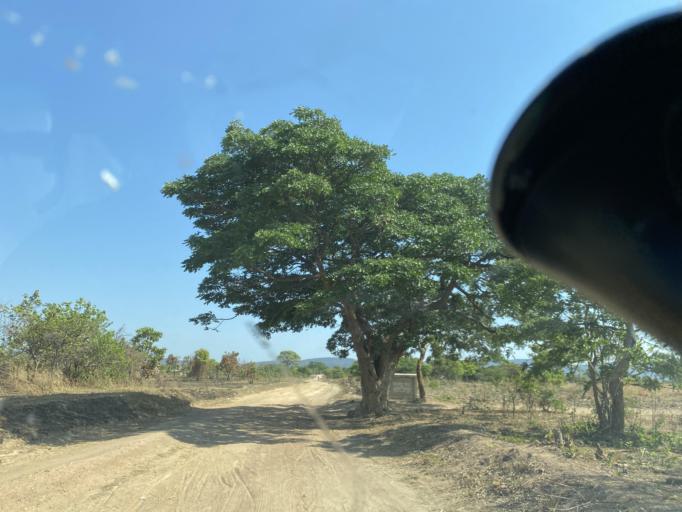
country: ZM
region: Lusaka
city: Chongwe
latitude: -15.2316
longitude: 28.8400
